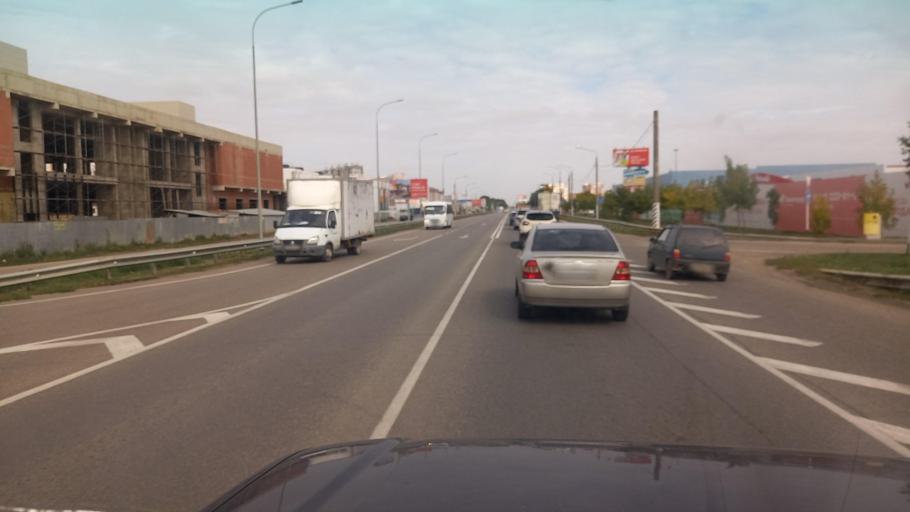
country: RU
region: Krasnodarskiy
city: Krasnodar
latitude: 45.0848
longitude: 38.9002
